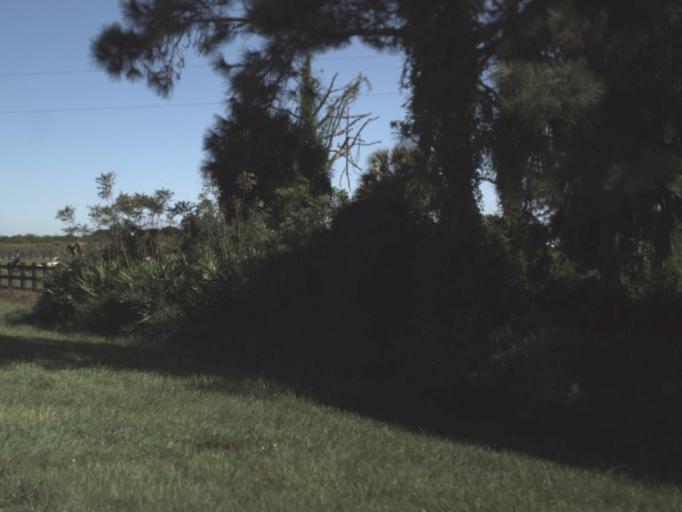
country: US
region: Florida
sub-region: Glades County
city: Moore Haven
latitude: 26.7684
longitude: -81.2372
